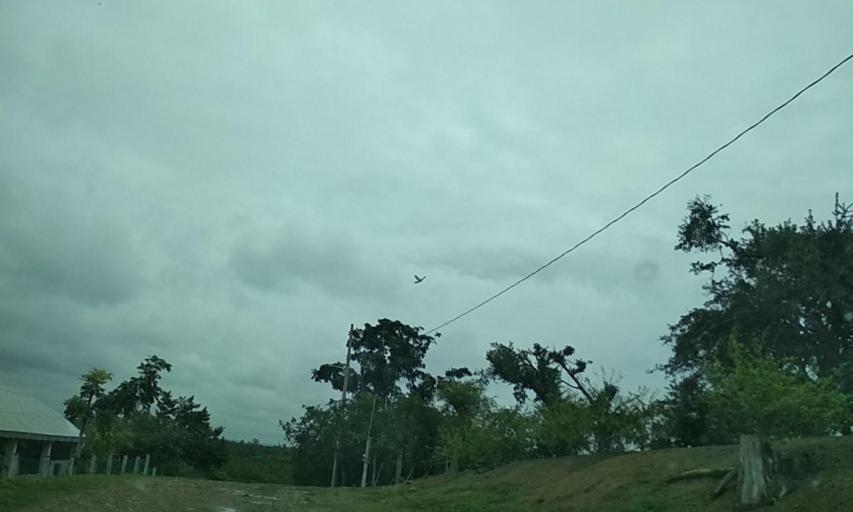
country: MX
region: Puebla
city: Espinal
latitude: 20.3213
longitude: -97.4160
